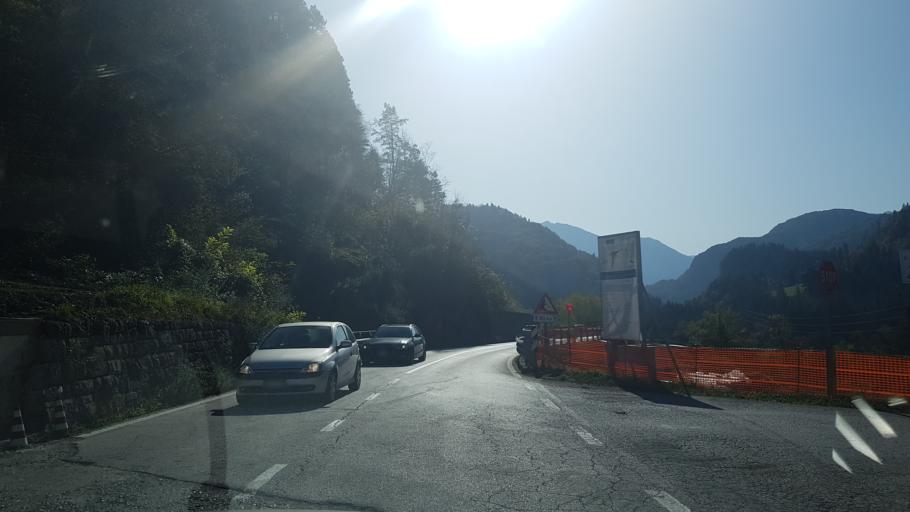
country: IT
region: Friuli Venezia Giulia
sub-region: Provincia di Udine
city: Ovaro
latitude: 46.4768
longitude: 12.8706
